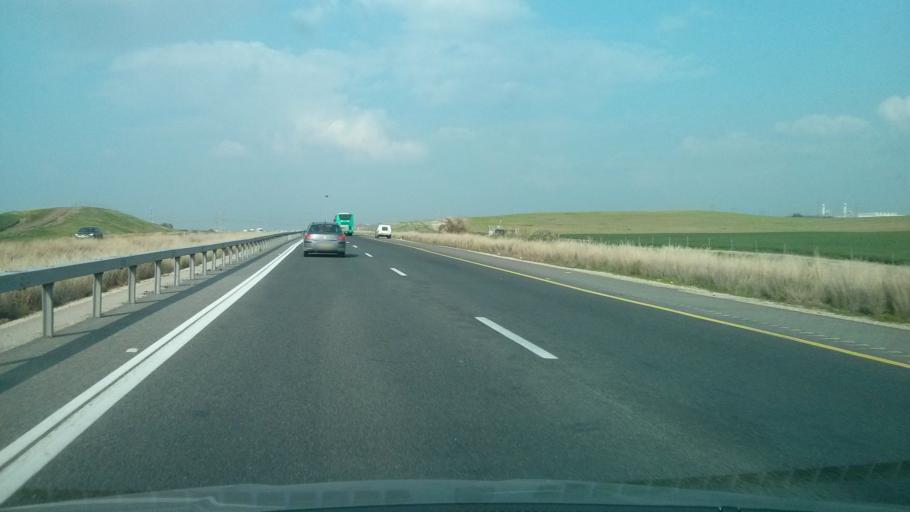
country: IL
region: Southern District
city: Qiryat Gat
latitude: 31.7008
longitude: 34.8173
